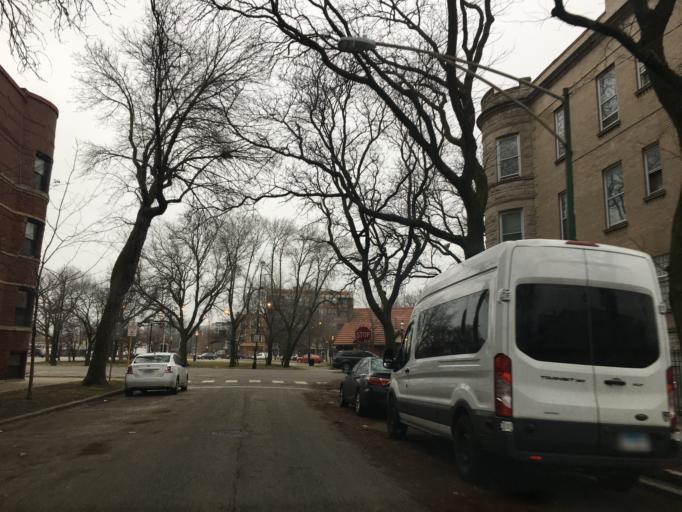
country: US
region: Illinois
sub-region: Cook County
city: Lincolnwood
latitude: 41.9293
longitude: -87.7061
